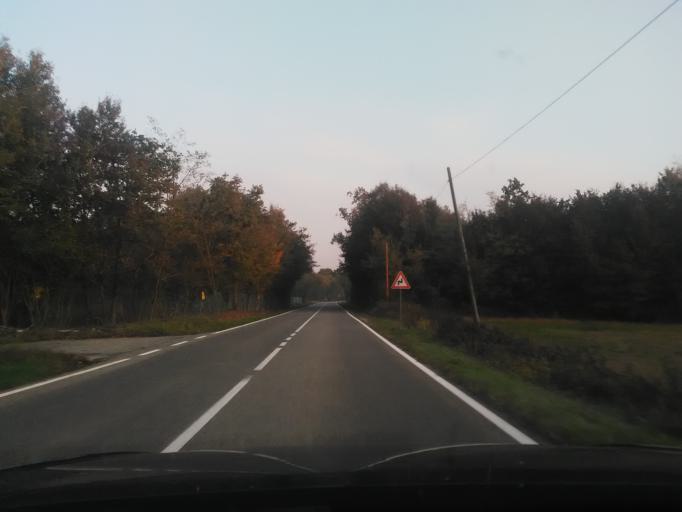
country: IT
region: Piedmont
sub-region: Provincia di Vercelli
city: San Maurizio
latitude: 45.5748
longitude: 8.2944
